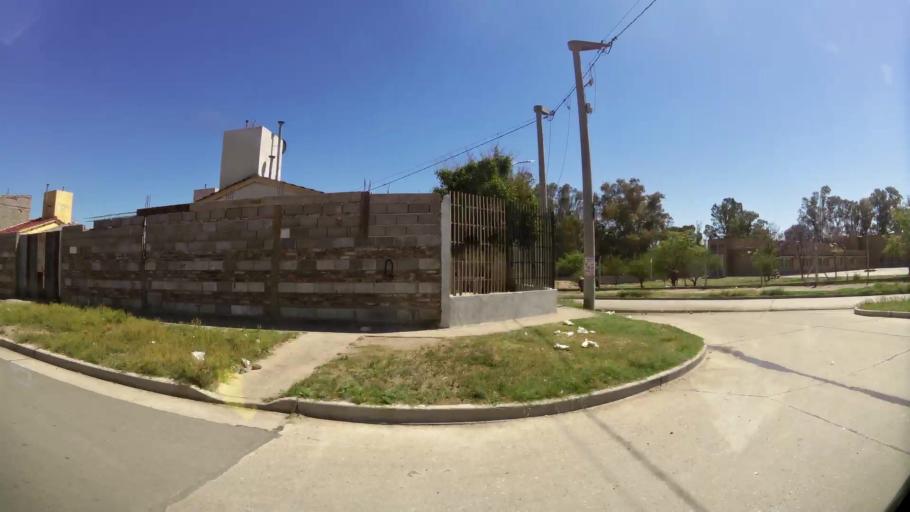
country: AR
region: Cordoba
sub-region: Departamento de Capital
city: Cordoba
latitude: -31.4102
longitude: -64.1337
